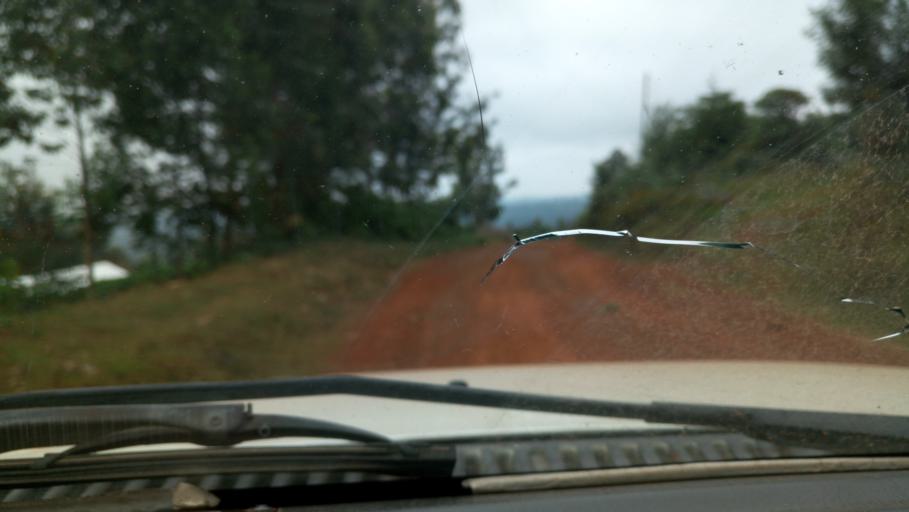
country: KE
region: Murang'a District
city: Kangema
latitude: -0.6390
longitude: 36.9329
